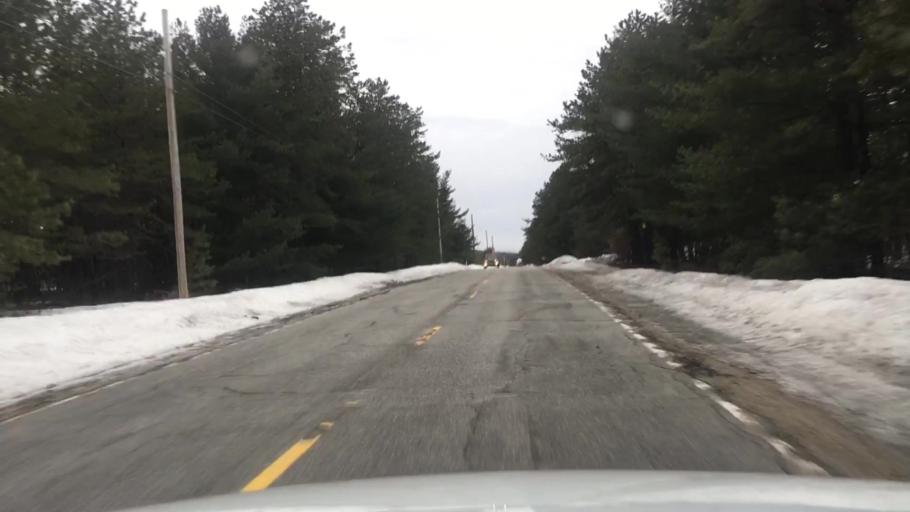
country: US
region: Maine
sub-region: York County
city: Shapleigh
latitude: 43.5853
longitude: -70.8746
